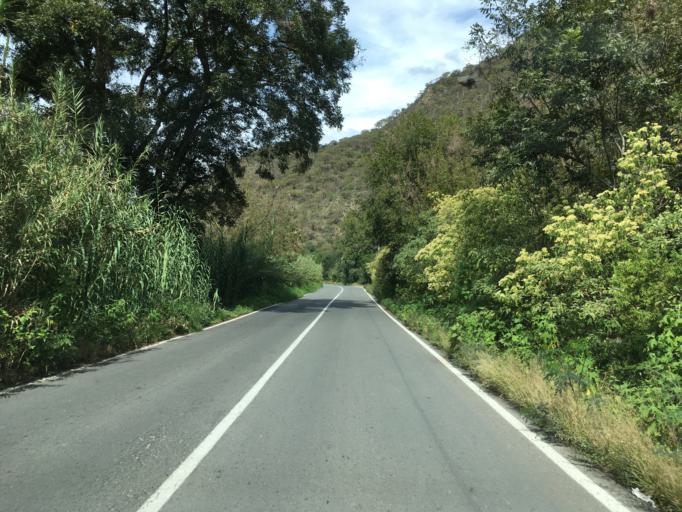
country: MX
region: Hidalgo
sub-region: San Agustin Metzquititlan
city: Mezquititlan
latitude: 20.5102
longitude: -98.7061
